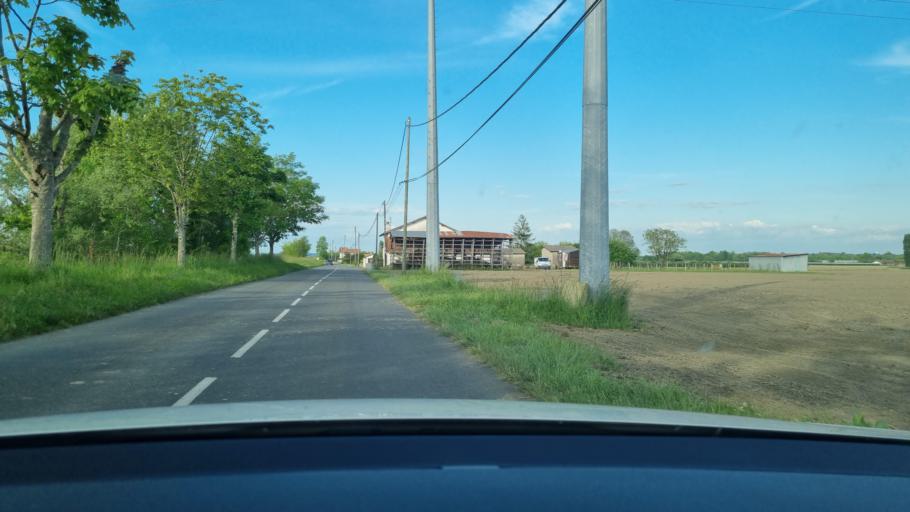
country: FR
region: Aquitaine
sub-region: Departement des Pyrenees-Atlantiques
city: Bardos
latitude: 43.5265
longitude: -1.2238
